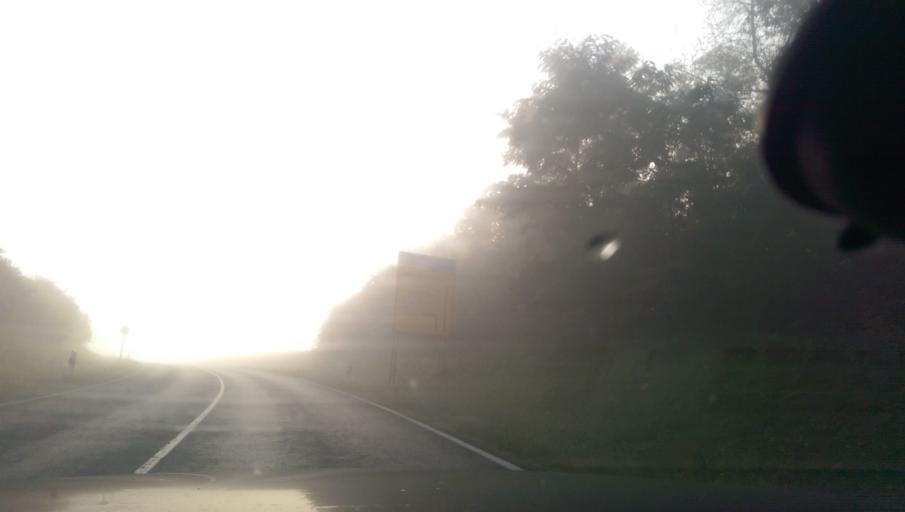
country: DE
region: Bavaria
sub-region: Regierungsbezirk Unterfranken
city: Oerlenbach
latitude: 50.1500
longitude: 10.1078
